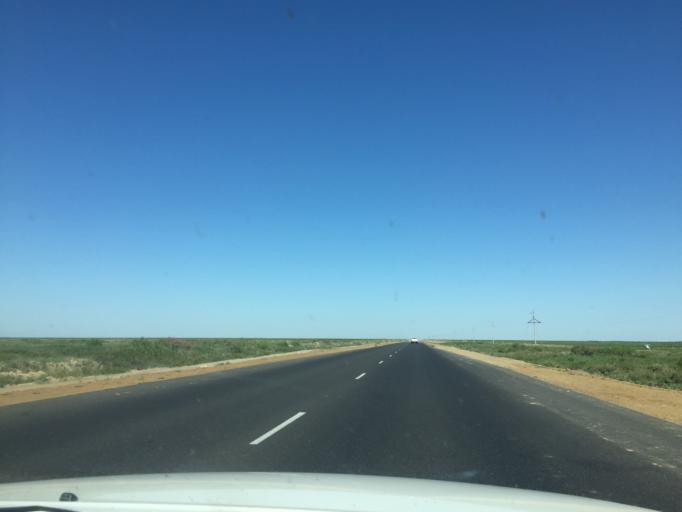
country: KZ
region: Qyzylorda
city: Dzhalagash
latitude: 44.9369
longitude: 64.6430
